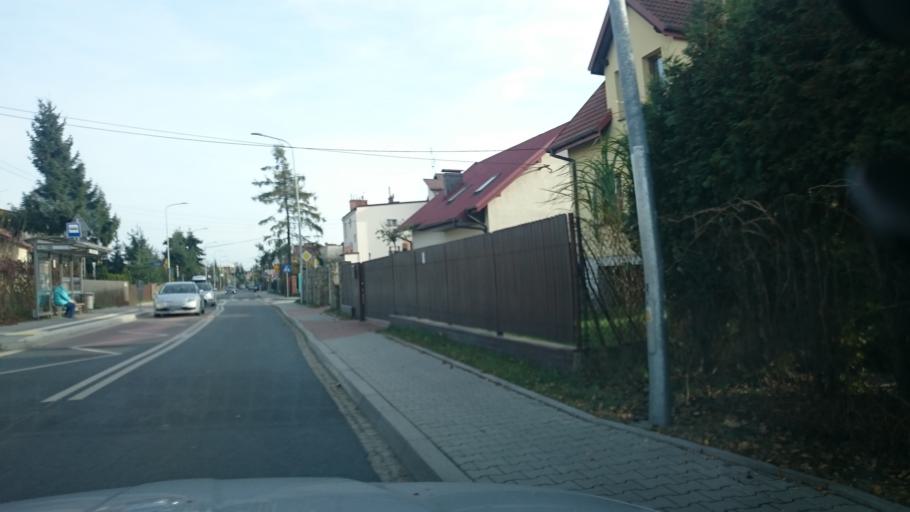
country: PL
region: Lesser Poland Voivodeship
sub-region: Powiat wielicki
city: Czarnochowice
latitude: 50.0213
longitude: 20.0159
